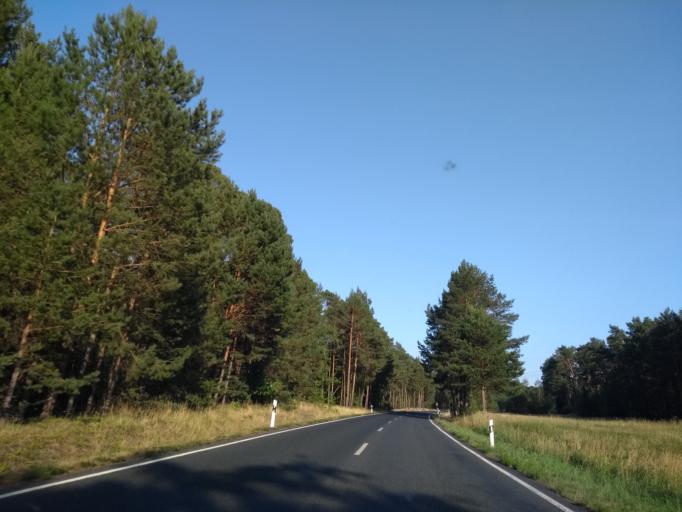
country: DE
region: Brandenburg
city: Lubbenau
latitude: 51.8572
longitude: 13.8745
